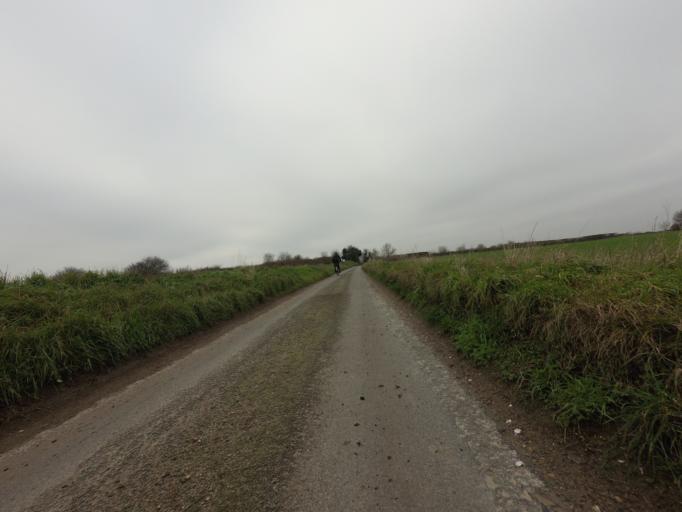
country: GB
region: England
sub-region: Kent
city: Dartford
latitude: 51.4128
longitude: 0.2280
